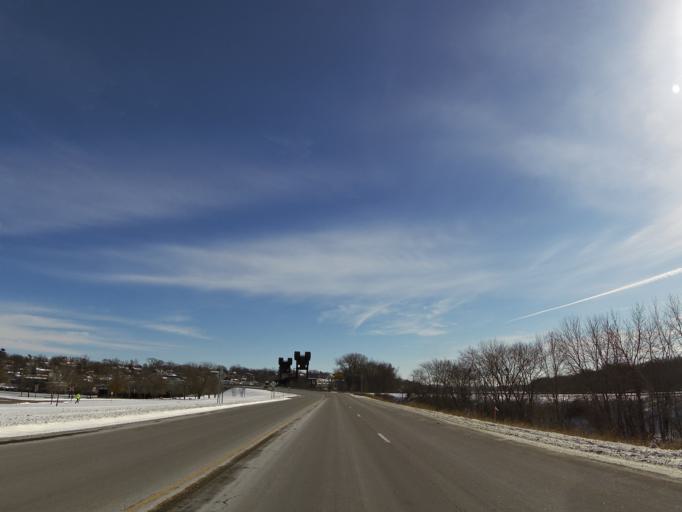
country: US
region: Wisconsin
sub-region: Pierce County
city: Prescott
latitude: 44.7488
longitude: -92.8100
